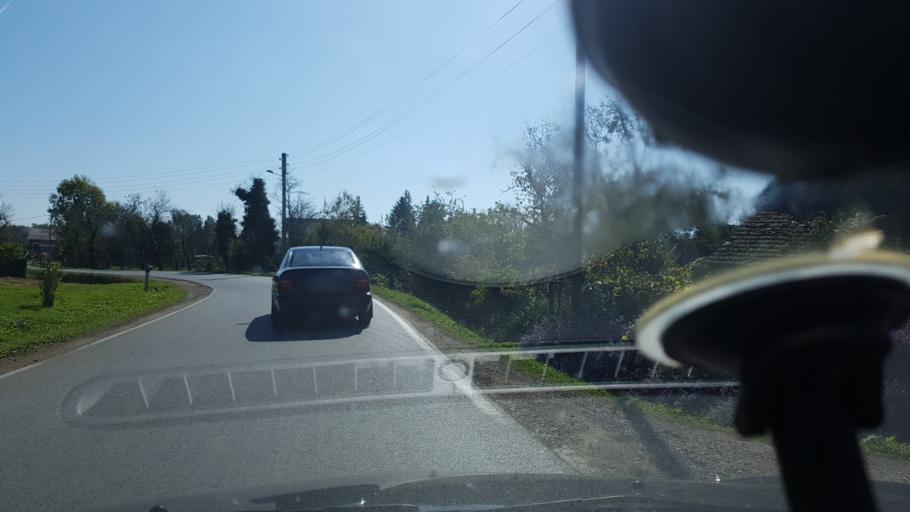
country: HR
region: Zagrebacka
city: Lupoglav
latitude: 45.7180
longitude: 16.3125
